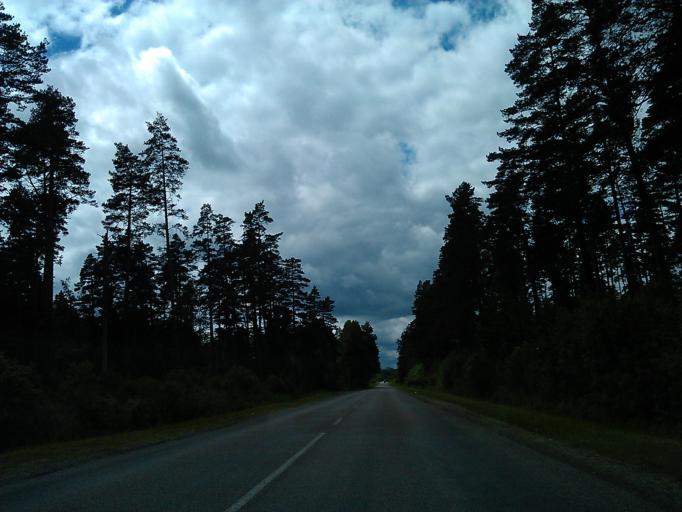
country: LV
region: Talsu Rajons
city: Stende
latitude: 57.0846
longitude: 22.3023
